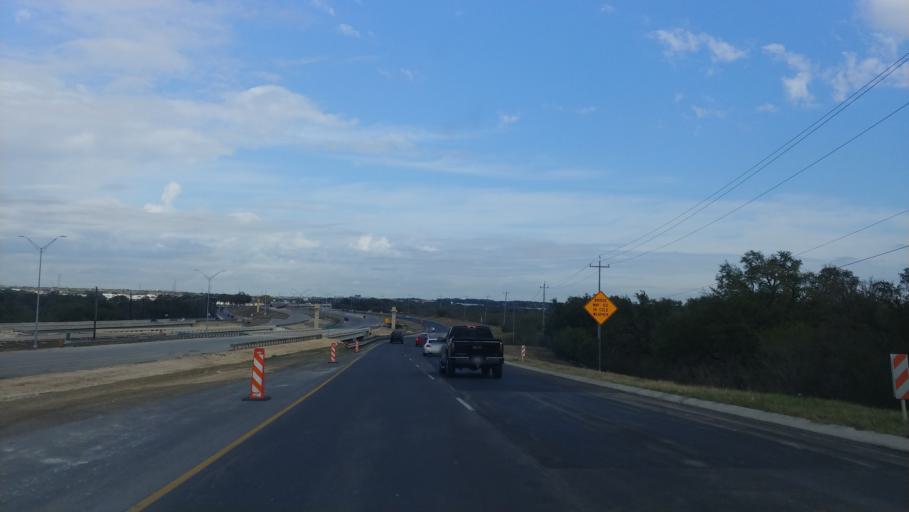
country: US
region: Texas
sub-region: Bexar County
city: Lackland Air Force Base
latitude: 29.4184
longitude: -98.7092
